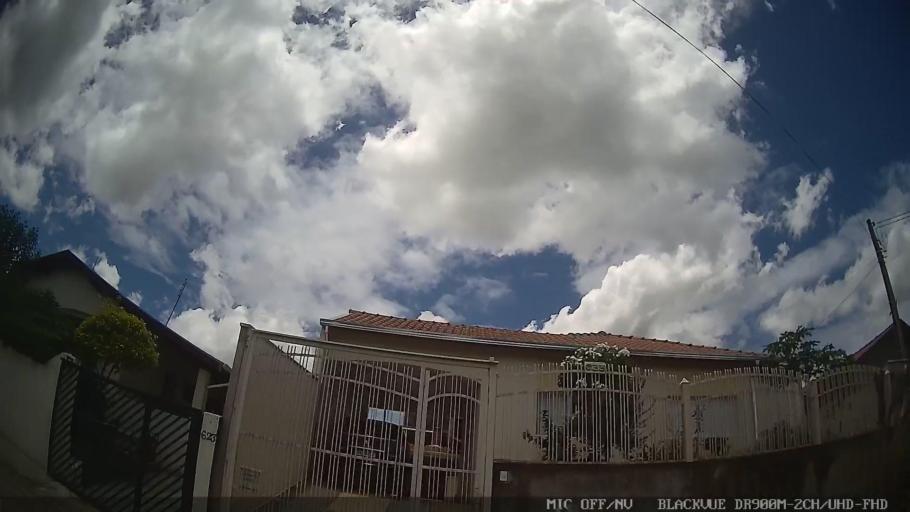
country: BR
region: Sao Paulo
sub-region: Jaguariuna
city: Jaguariuna
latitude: -22.7155
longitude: -46.9793
